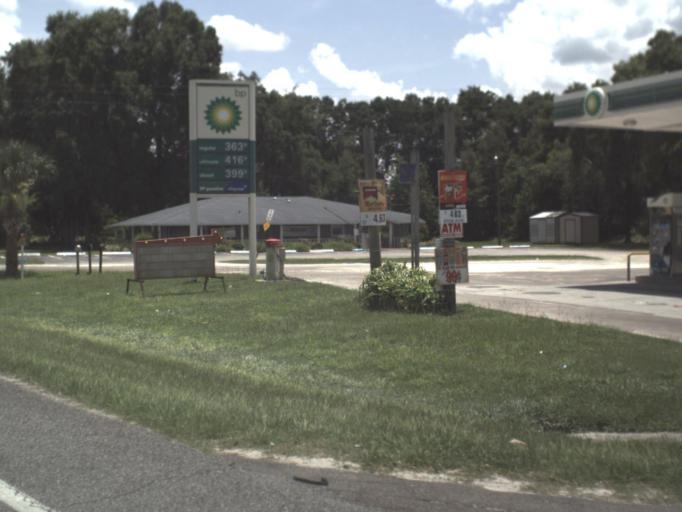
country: US
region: Florida
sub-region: Levy County
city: Manatee Road
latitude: 29.5272
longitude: -82.8859
